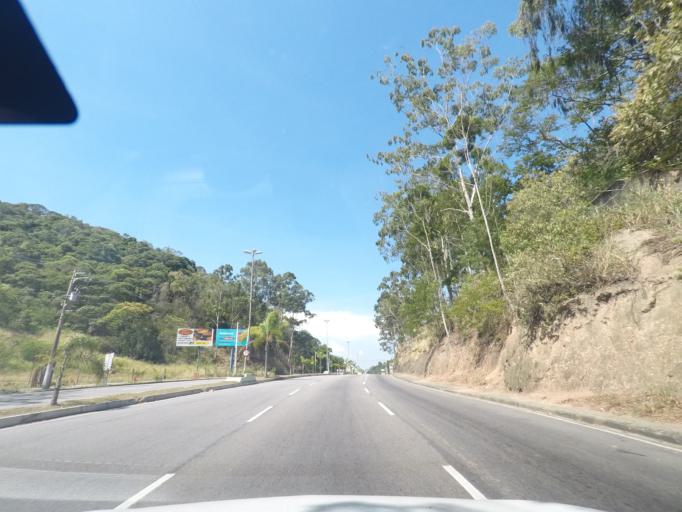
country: BR
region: Rio de Janeiro
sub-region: Niteroi
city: Niteroi
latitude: -22.9207
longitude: -43.0536
